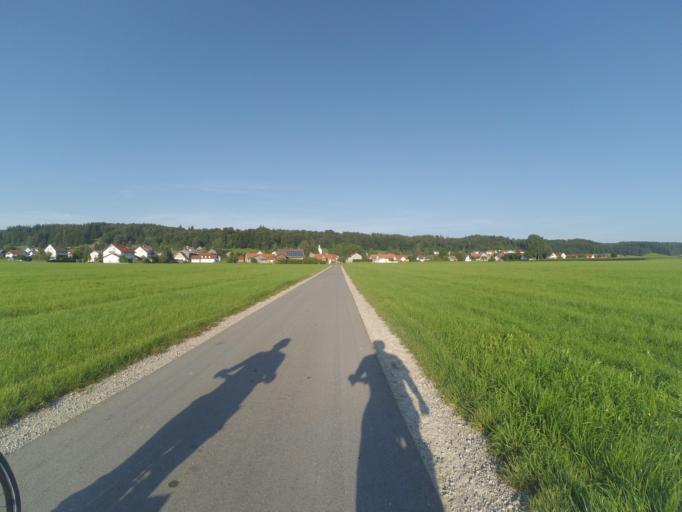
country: DE
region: Bavaria
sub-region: Swabia
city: Dirlewang
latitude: 48.0083
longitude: 10.5317
